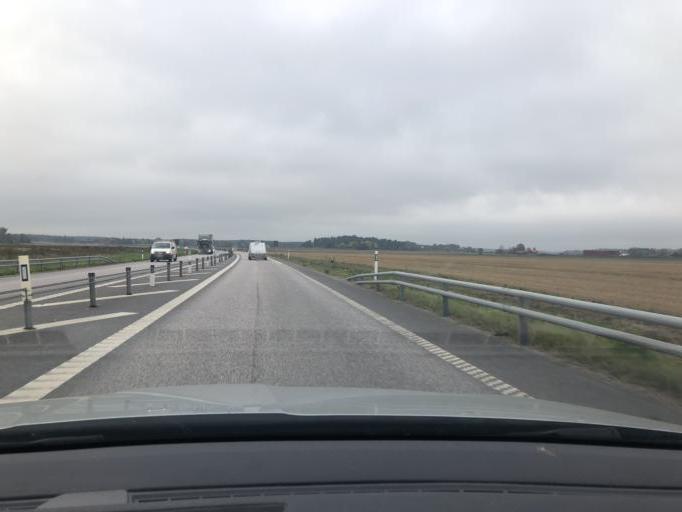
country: SE
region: Uppsala
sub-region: Uppsala Kommun
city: Vattholma
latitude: 59.9466
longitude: 17.8475
